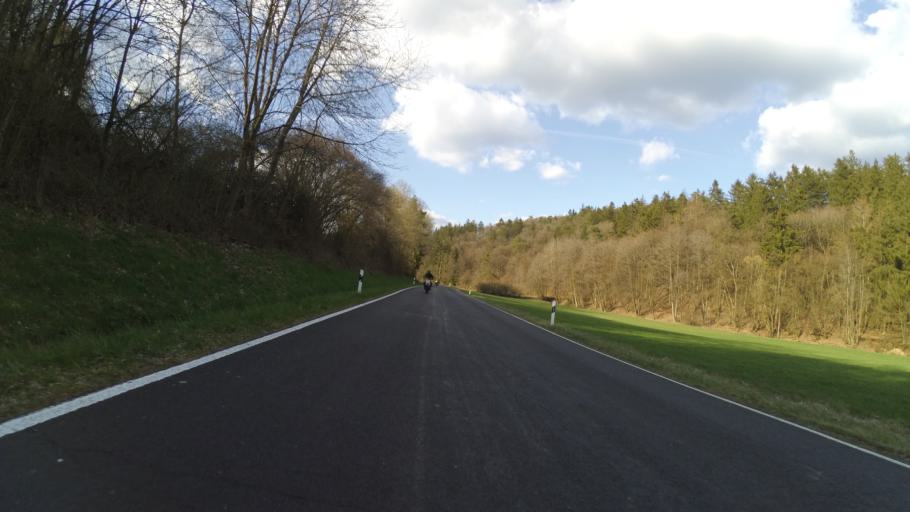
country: DE
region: Rheinland-Pfalz
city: Steiningen
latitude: 50.1899
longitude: 6.9073
